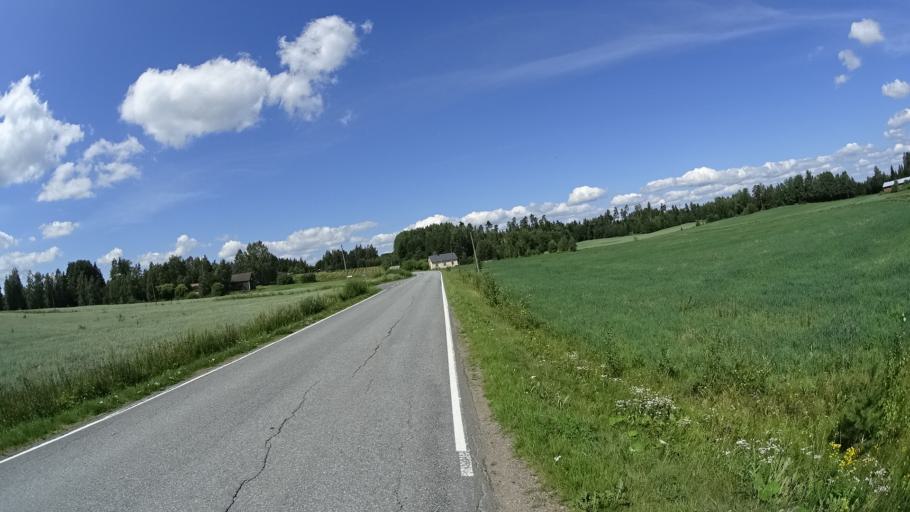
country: FI
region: Haeme
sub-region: Forssa
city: Tammela
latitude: 60.7620
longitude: 23.8821
